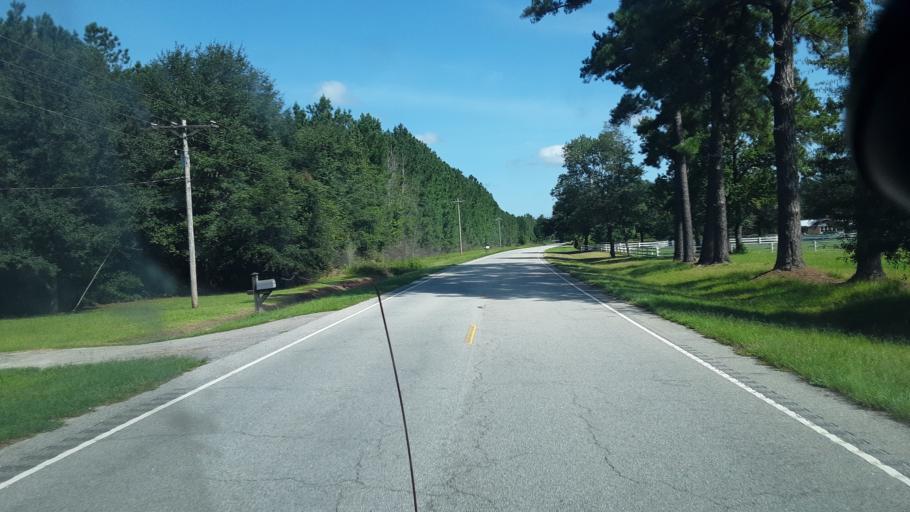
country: US
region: South Carolina
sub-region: Hampton County
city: Varnville
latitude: 32.7677
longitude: -81.0510
